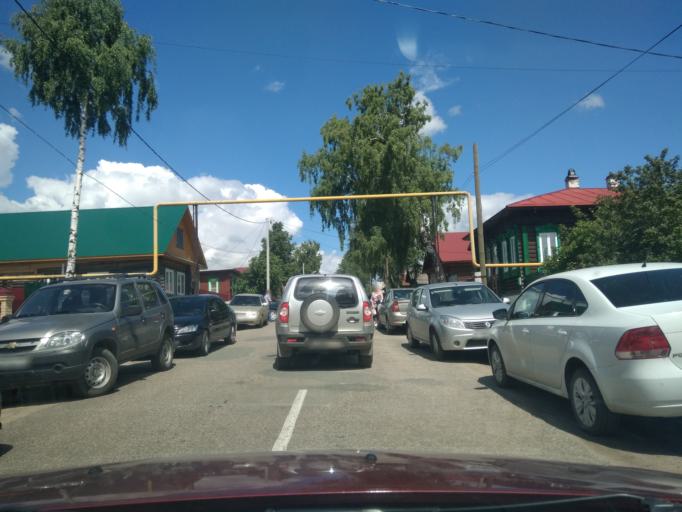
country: RU
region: Vladimir
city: Melenki
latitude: 55.3395
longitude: 41.6362
